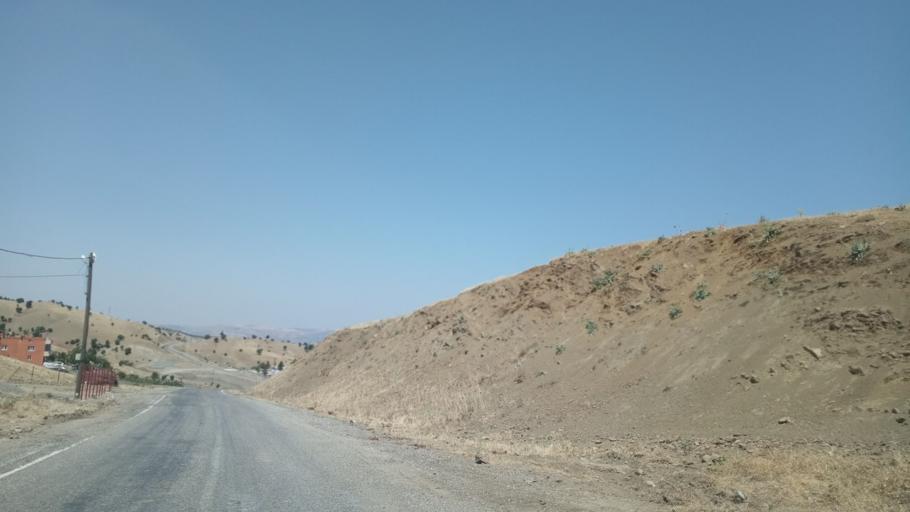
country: TR
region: Siirt
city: Dilektepe
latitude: 38.0759
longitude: 41.8279
